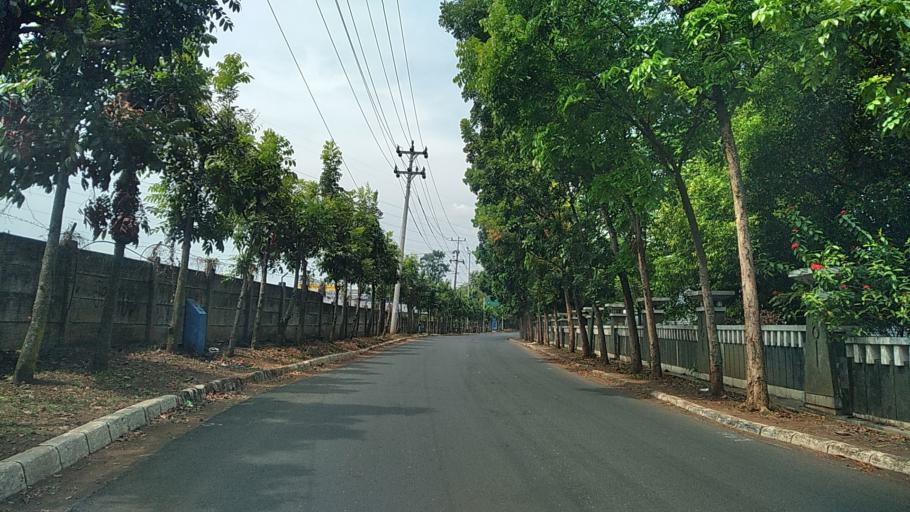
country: ID
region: Central Java
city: Semarang
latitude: -7.0519
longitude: 110.4329
